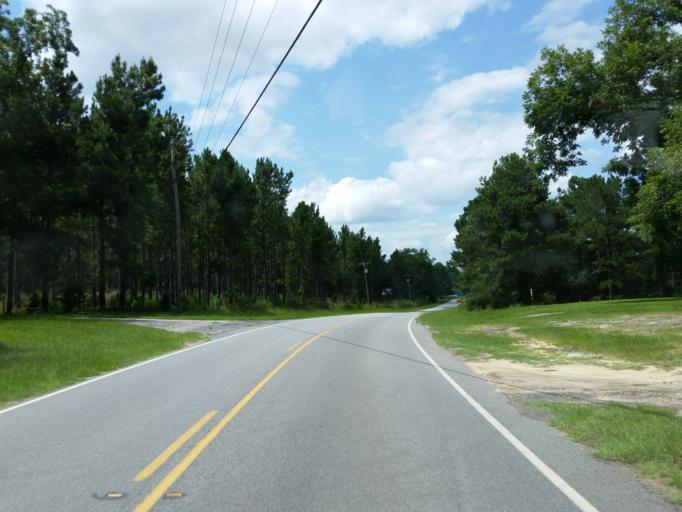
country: US
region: Georgia
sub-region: Tift County
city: Unionville
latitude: 31.4003
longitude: -83.5179
